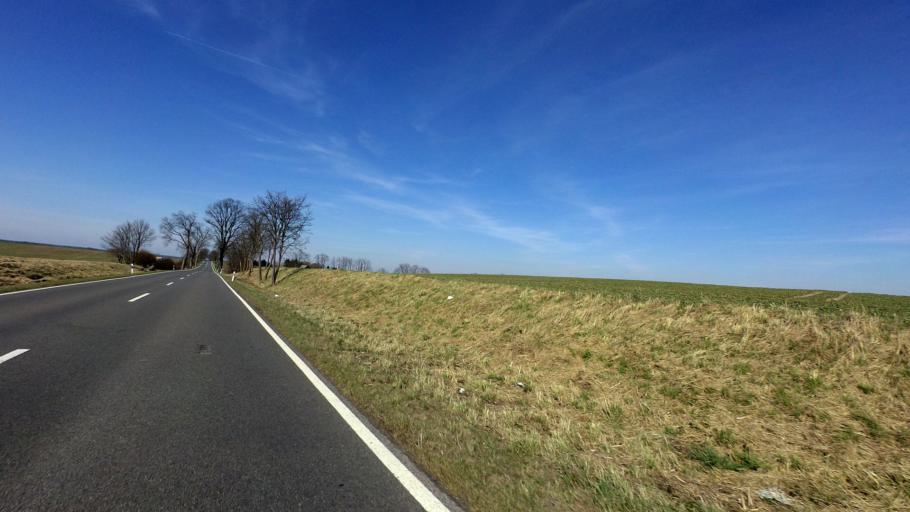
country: DE
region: Brandenburg
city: Protzel
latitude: 52.6109
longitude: 14.0212
